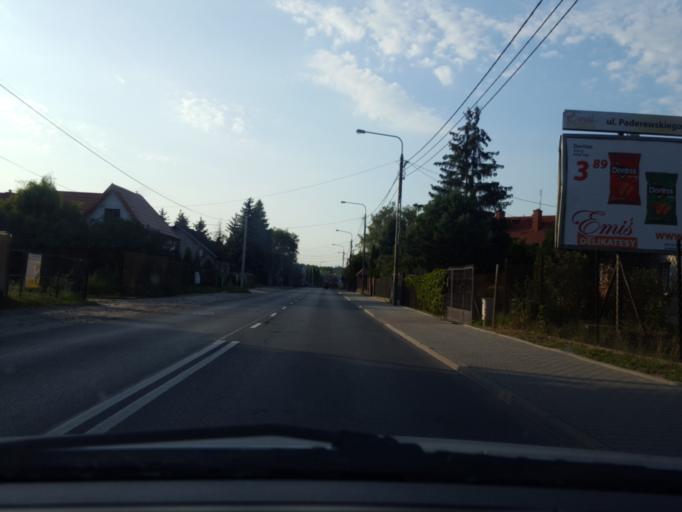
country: PL
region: Masovian Voivodeship
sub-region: Warszawa
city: Rembertow
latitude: 52.2691
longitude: 21.1518
